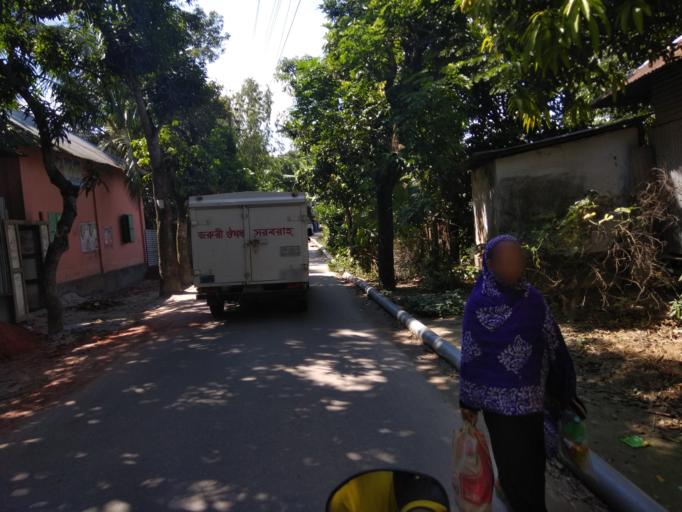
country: BD
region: Dhaka
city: Narayanganj
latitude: 23.4401
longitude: 90.4823
